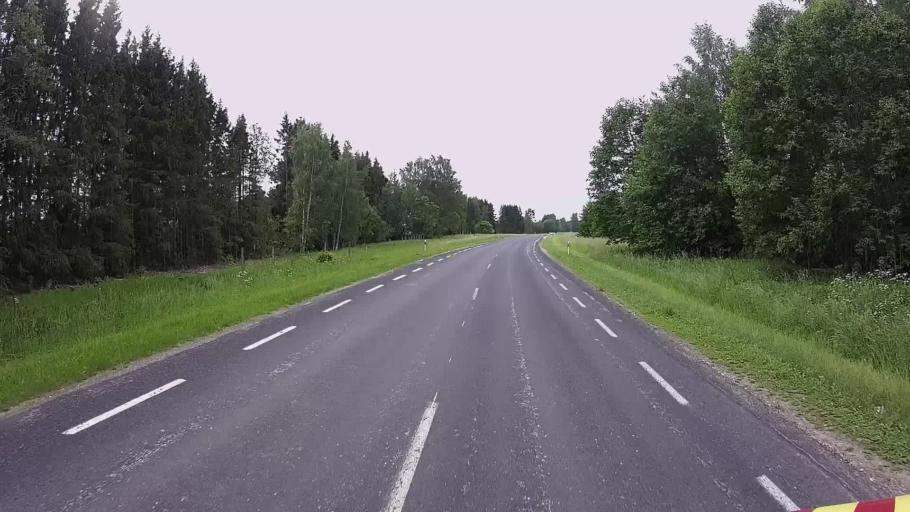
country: EE
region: Viljandimaa
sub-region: Karksi vald
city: Karksi-Nuia
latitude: 58.2042
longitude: 25.6204
